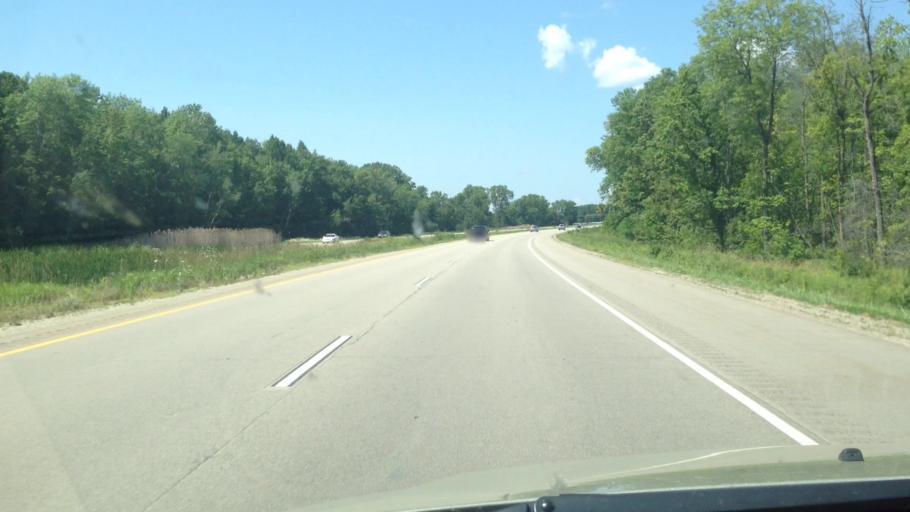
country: US
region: Wisconsin
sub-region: Oconto County
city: Oconto
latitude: 44.8022
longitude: -87.9842
